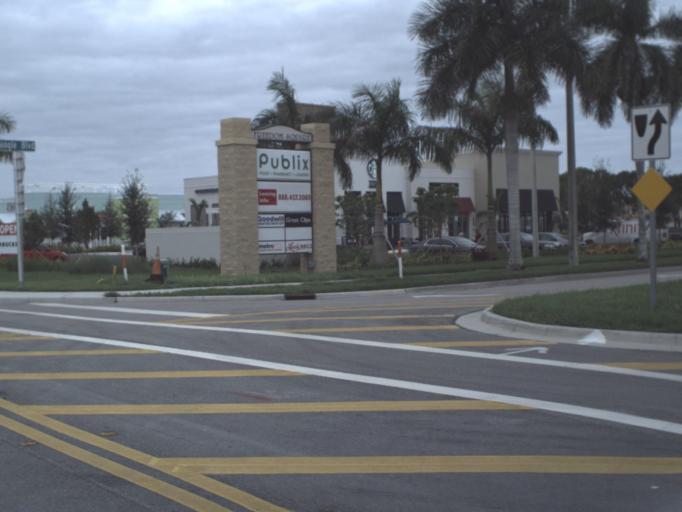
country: US
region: Florida
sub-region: Collier County
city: Lely Resort
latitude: 26.0669
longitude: -81.6967
